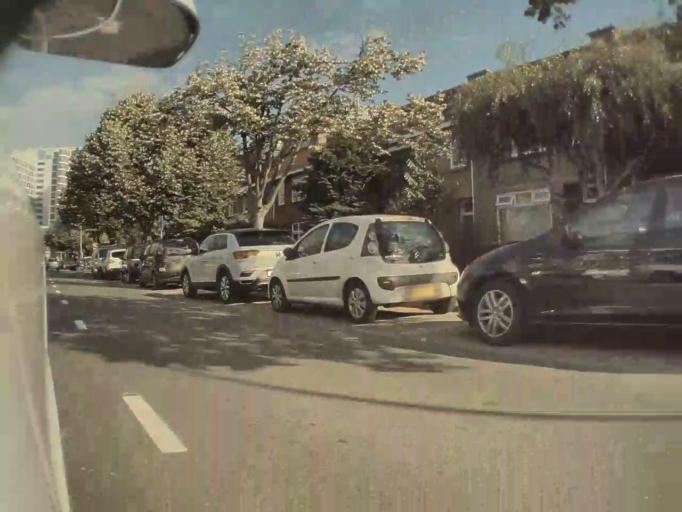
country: NL
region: South Holland
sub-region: Gemeente Leidschendam-Voorburg
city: Voorburg
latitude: 52.0759
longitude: 4.3410
